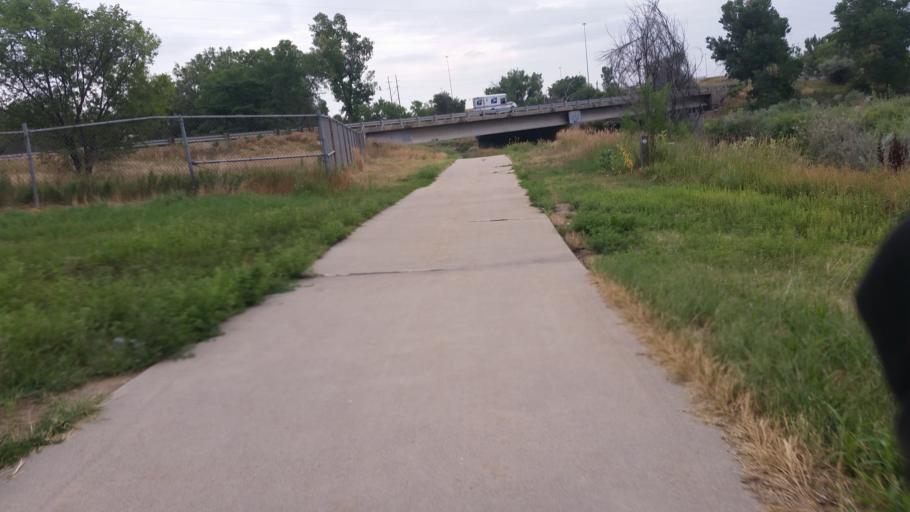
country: US
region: Colorado
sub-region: Adams County
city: Twin Lakes
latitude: 39.8196
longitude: -104.9882
